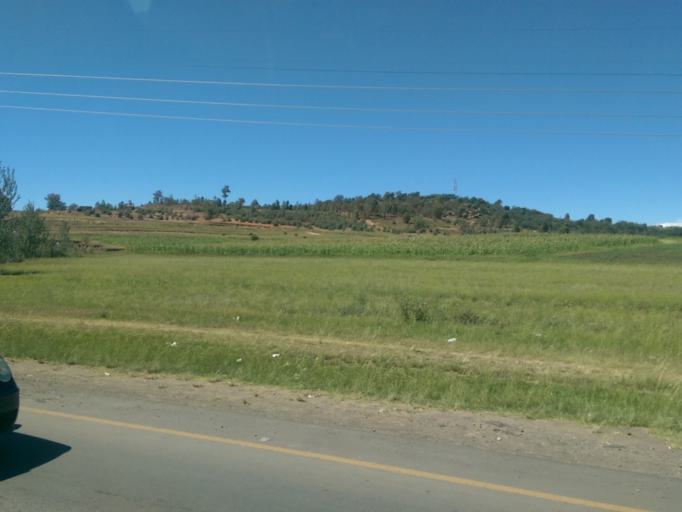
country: LS
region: Maseru
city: Maseru
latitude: -29.3999
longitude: 27.5552
